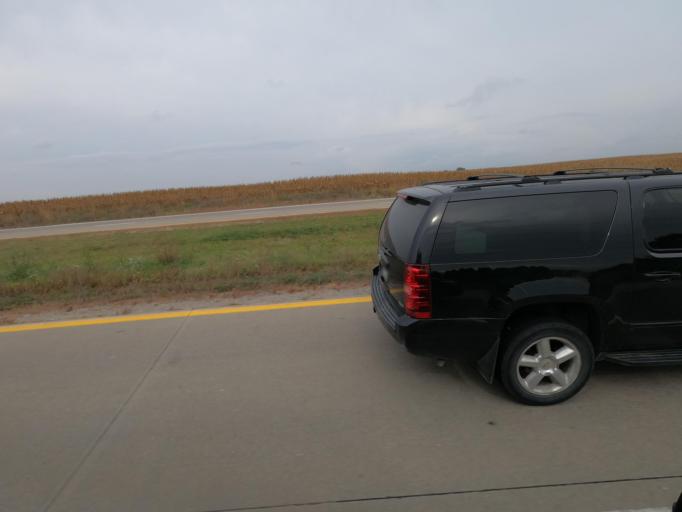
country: US
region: Iowa
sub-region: Mahaska County
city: Oskaloosa
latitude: 41.3542
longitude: -92.7621
